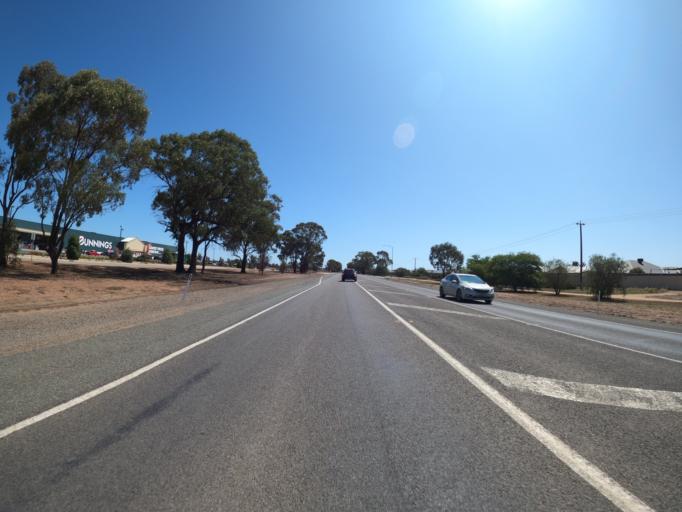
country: AU
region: Victoria
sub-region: Moira
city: Yarrawonga
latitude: -36.0110
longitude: 146.0267
